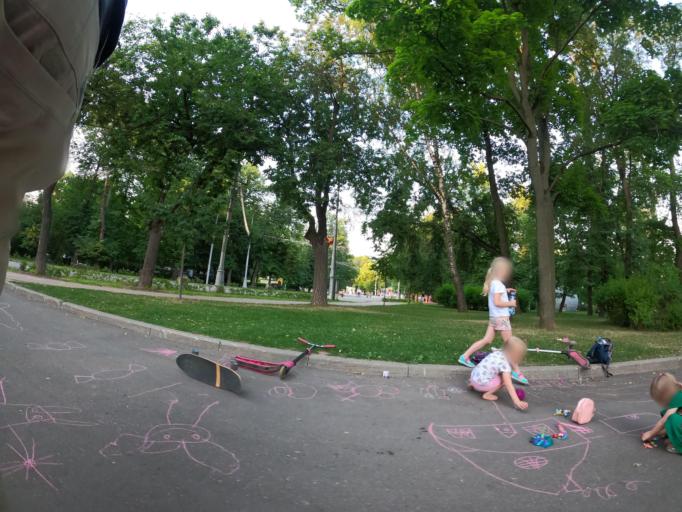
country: RU
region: Moscow
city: Sokol'niki
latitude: 55.7936
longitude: 37.6753
